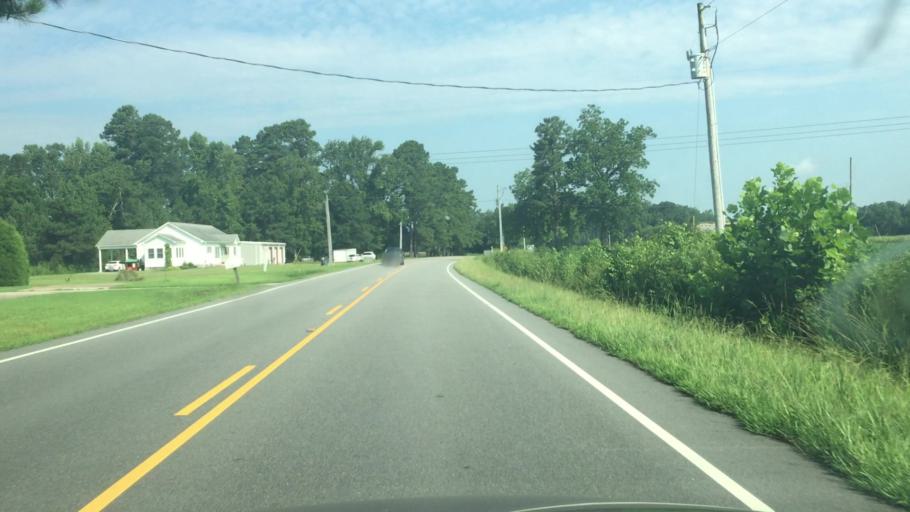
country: US
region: North Carolina
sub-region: Columbus County
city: Chadbourn
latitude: 34.2905
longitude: -78.8246
